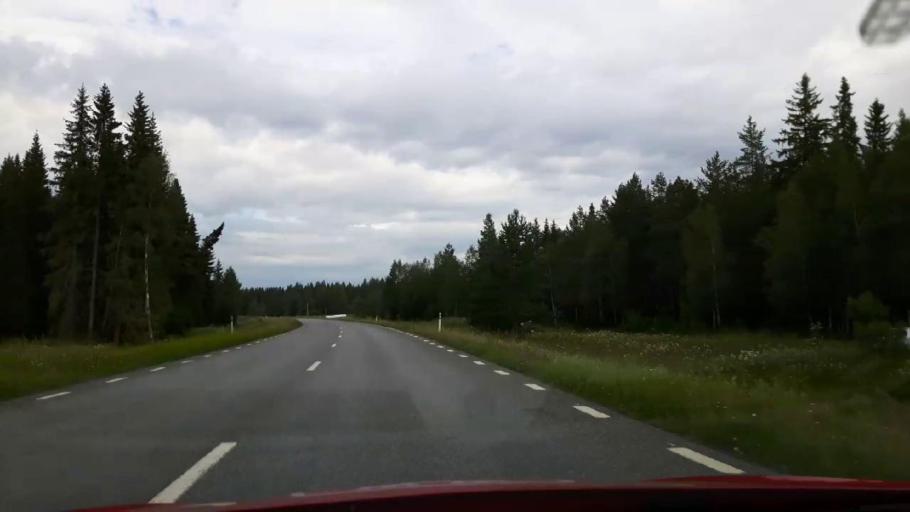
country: SE
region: Jaemtland
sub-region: Stroemsunds Kommun
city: Stroemsund
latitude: 63.5559
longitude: 15.3731
